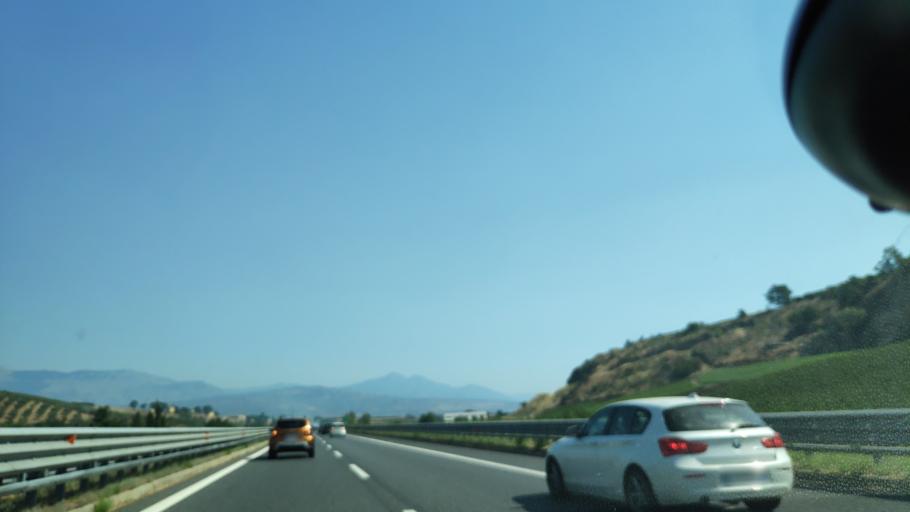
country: IT
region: Calabria
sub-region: Provincia di Cosenza
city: San Lorenzo del Vallo
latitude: 39.6972
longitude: 16.2379
